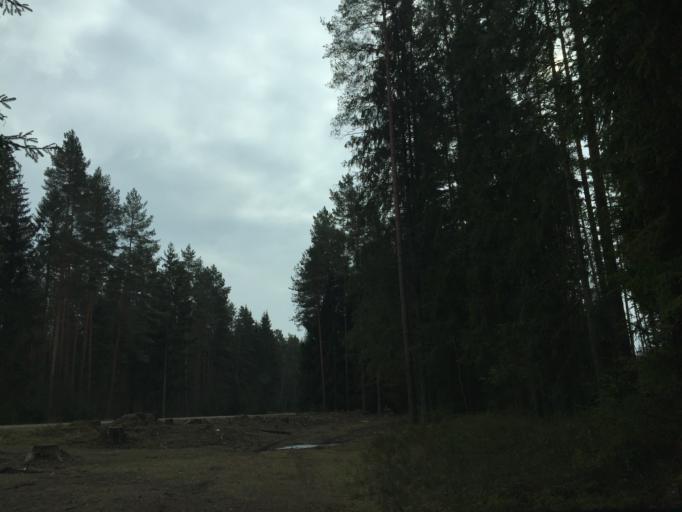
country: LV
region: Kekava
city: Kekava
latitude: 56.7657
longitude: 24.1570
